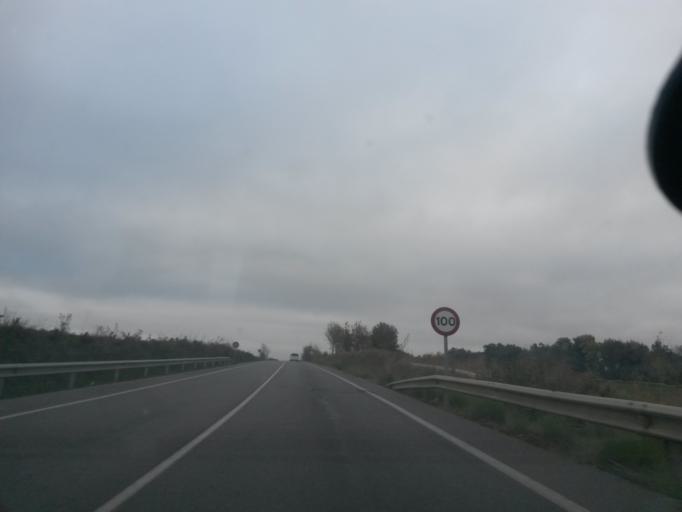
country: ES
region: Catalonia
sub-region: Provincia de Girona
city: Banyoles
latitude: 42.1251
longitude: 2.7820
